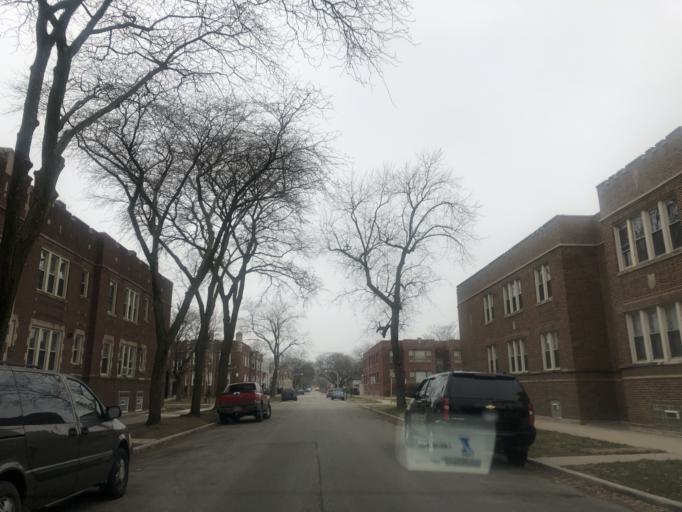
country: US
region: Illinois
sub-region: Cook County
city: Evergreen Park
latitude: 41.7492
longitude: -87.6173
